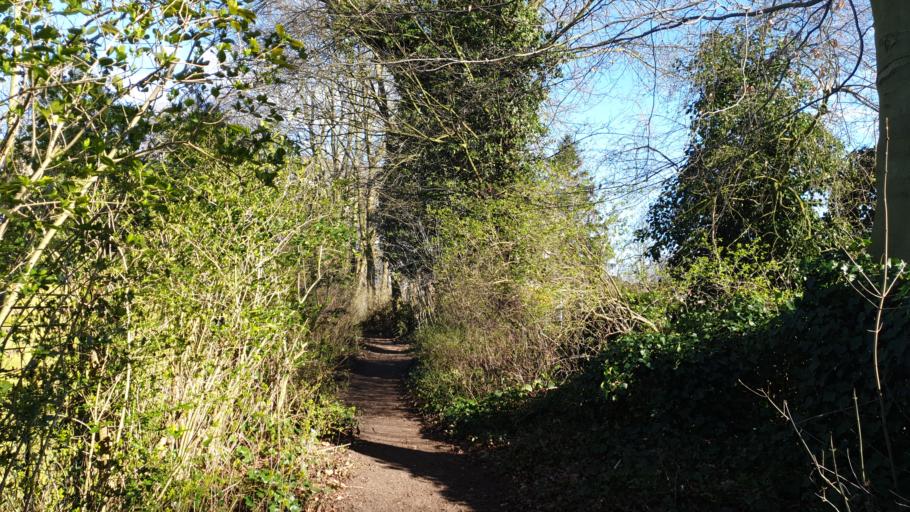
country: DE
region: Hamburg
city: Hamburg-Nord
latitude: 53.5868
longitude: 9.9625
